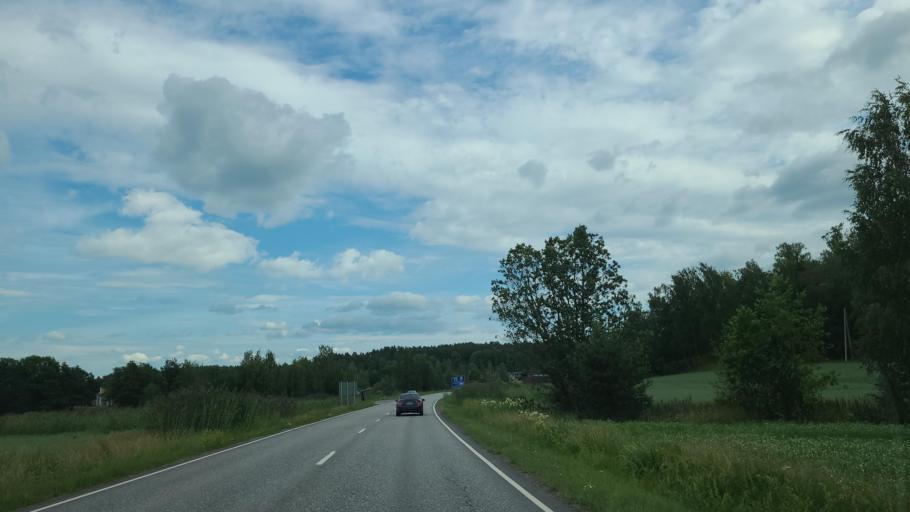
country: FI
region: Varsinais-Suomi
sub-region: Turku
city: Rymaettylae
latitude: 60.3806
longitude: 21.9414
